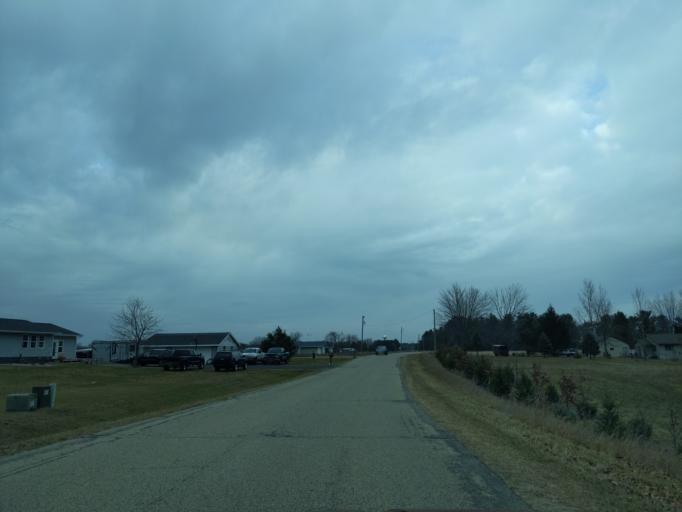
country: US
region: Wisconsin
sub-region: Waushara County
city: Wautoma
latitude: 44.0516
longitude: -89.2778
